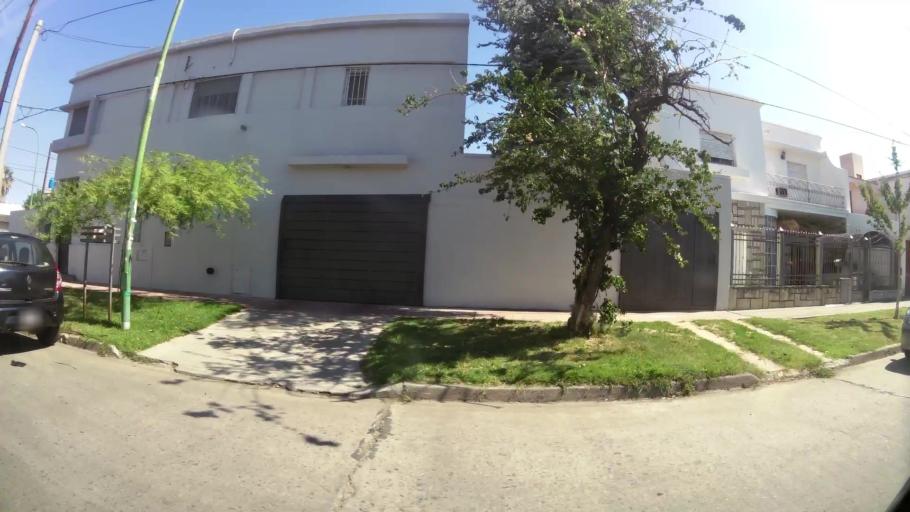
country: AR
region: Cordoba
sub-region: Departamento de Capital
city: Cordoba
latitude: -31.4183
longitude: -64.1673
